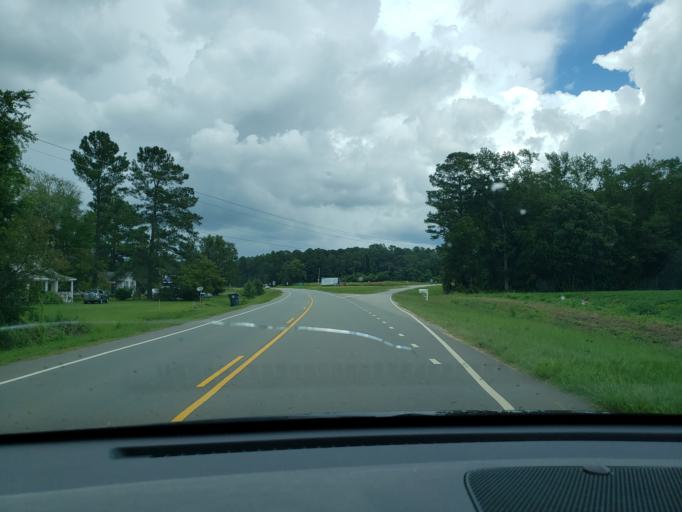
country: US
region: North Carolina
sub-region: Columbus County
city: Whiteville
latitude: 34.4675
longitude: -78.6715
